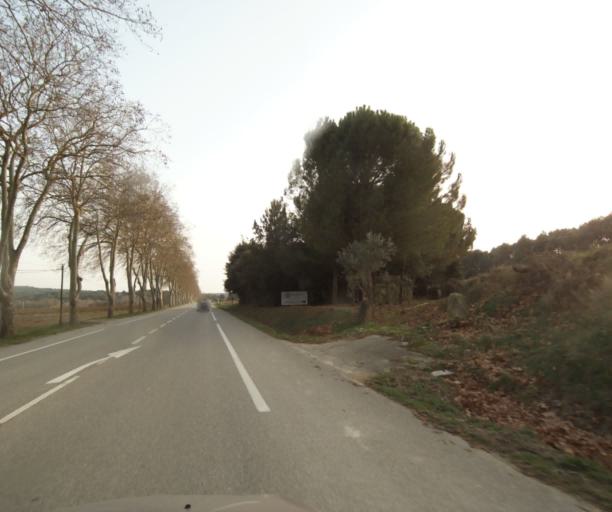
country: FR
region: Provence-Alpes-Cote d'Azur
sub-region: Departement des Bouches-du-Rhone
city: Rognes
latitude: 43.6498
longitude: 5.3578
